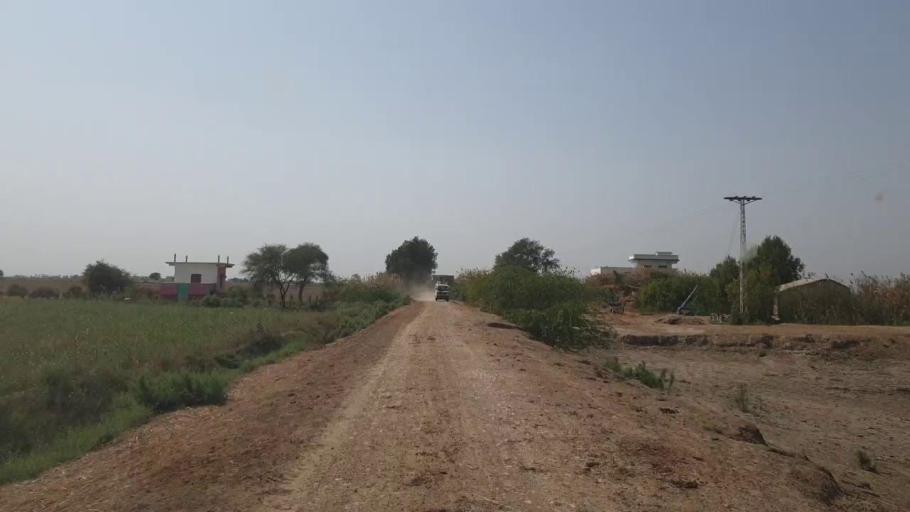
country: PK
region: Sindh
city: Jati
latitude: 24.4920
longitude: 68.5275
